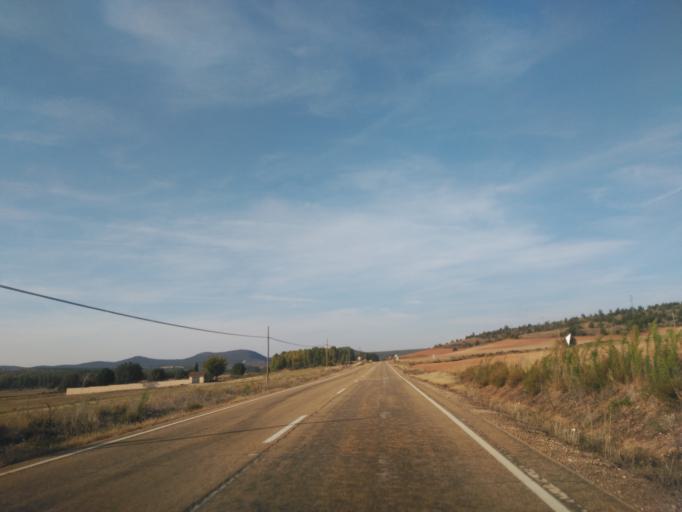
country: ES
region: Castille and Leon
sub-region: Provincia de Soria
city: Valdemaluque
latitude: 41.6790
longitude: -3.0448
